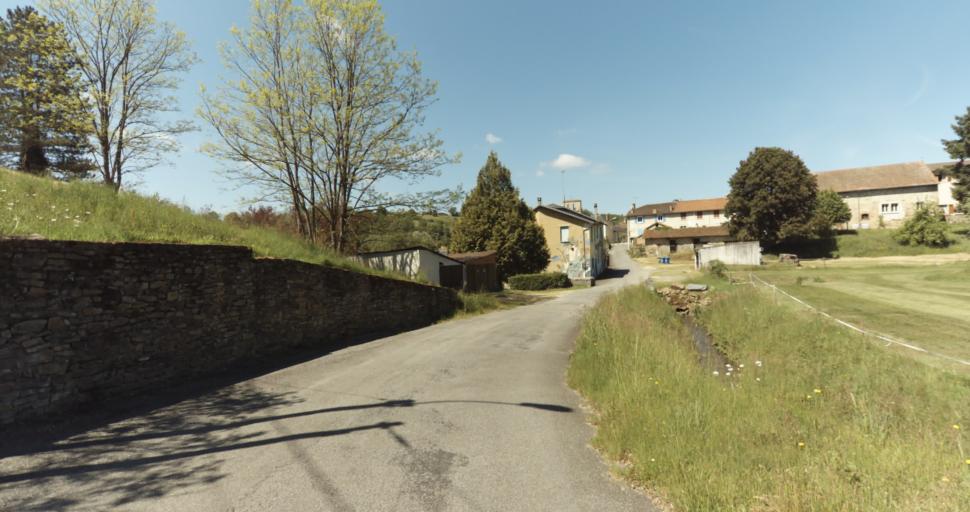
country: FR
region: Limousin
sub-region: Departement de la Haute-Vienne
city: Le Vigen
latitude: 45.7509
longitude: 1.2910
